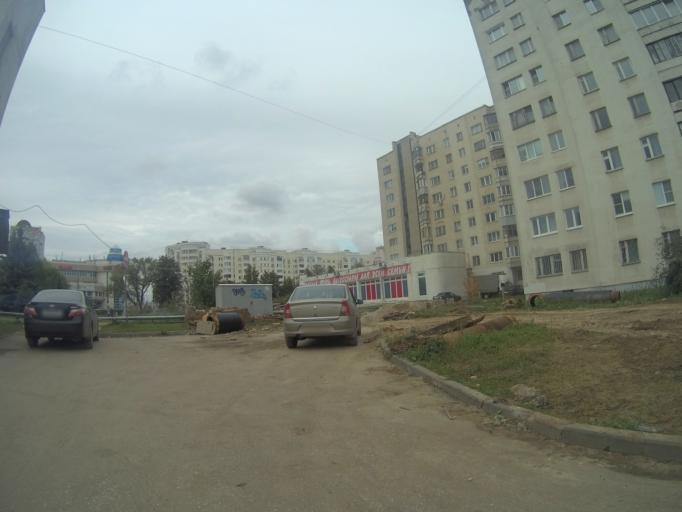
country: RU
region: Vladimir
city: Vladimir
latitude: 56.1171
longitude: 40.3534
